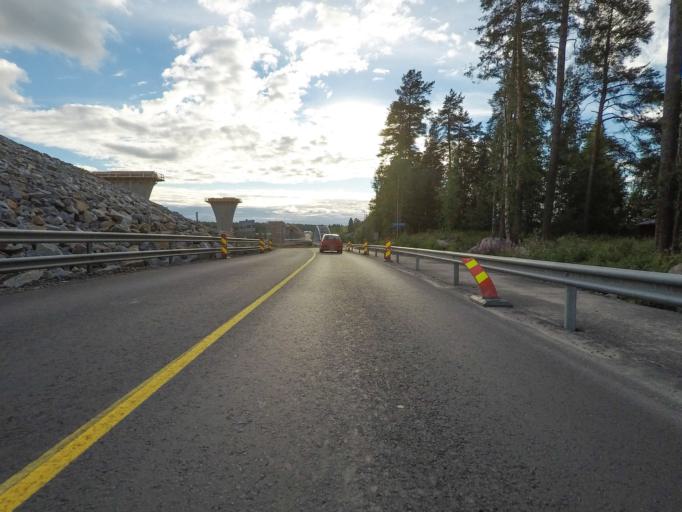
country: FI
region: Northern Savo
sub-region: Kuopio
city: Kuopio
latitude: 62.9704
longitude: 27.8382
